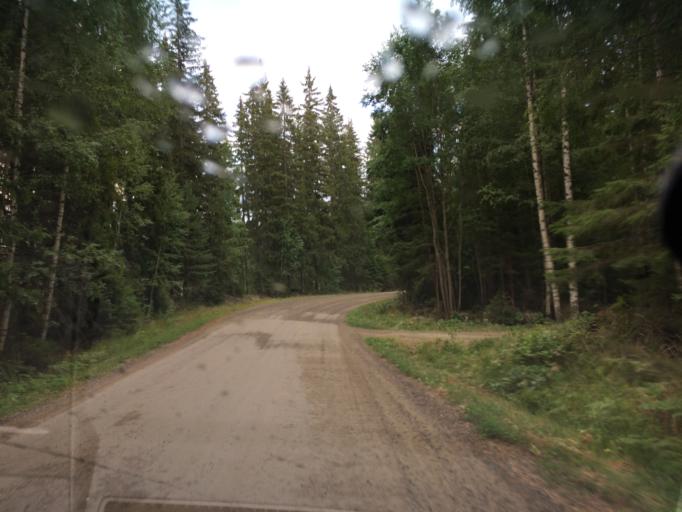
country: FI
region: Pirkanmaa
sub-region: Tampere
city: Luopioinen
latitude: 61.2720
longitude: 24.6739
